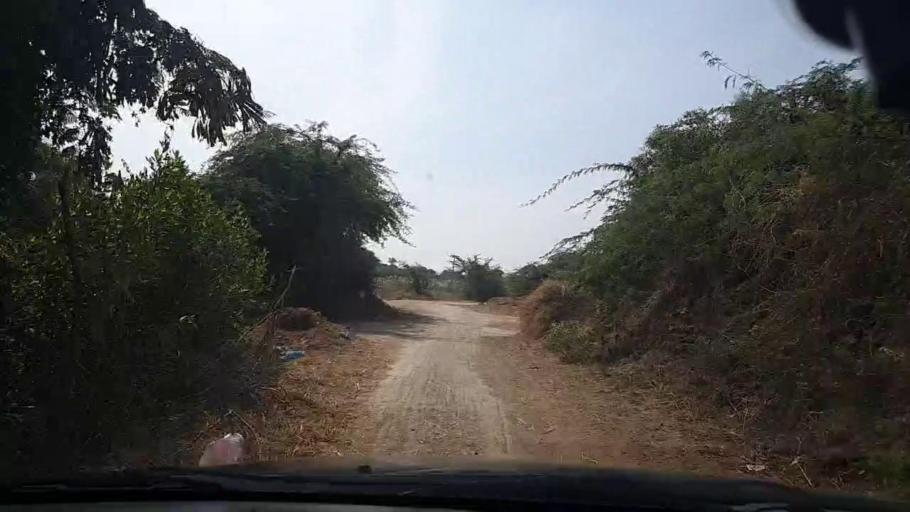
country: PK
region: Sindh
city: Mirpur Batoro
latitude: 24.7375
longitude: 68.2701
